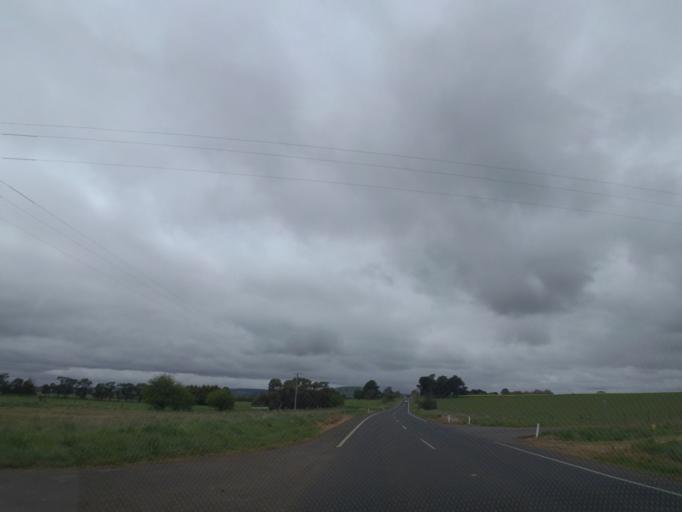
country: AU
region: Victoria
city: Brown Hill
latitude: -37.4103
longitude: 143.9753
